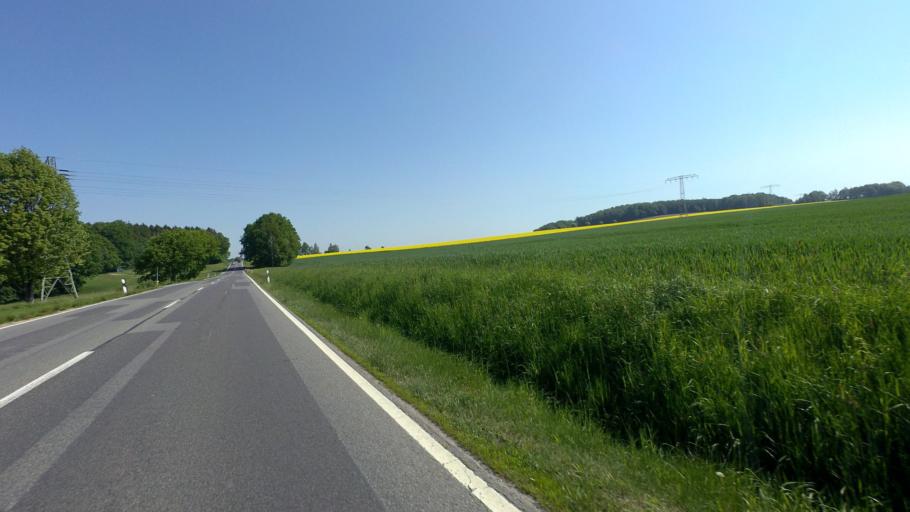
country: DE
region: Saxony
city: Rammenau
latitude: 51.1630
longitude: 14.1430
